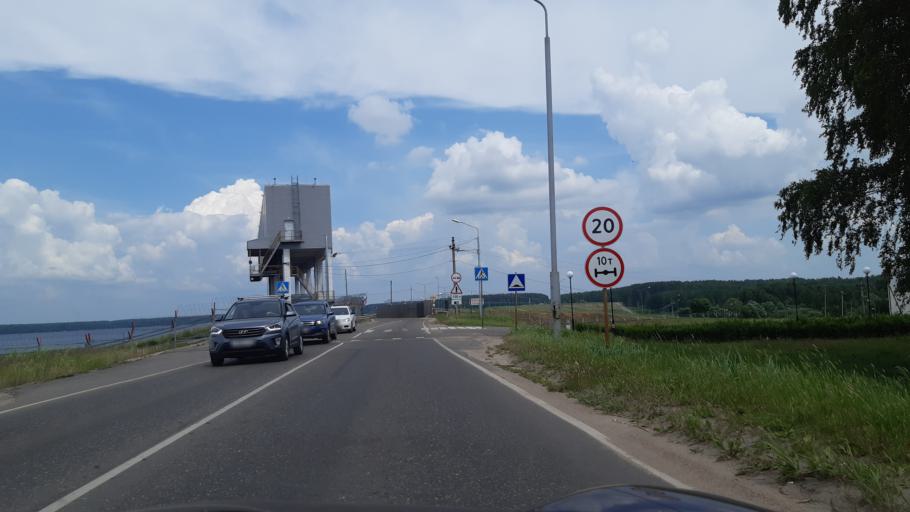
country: RU
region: Smolensk
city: Desnogorsk
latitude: 54.1555
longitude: 33.3059
